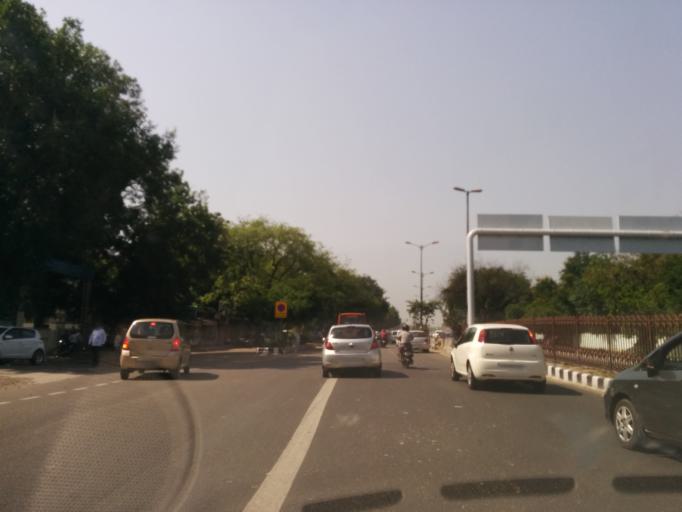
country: IN
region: NCT
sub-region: New Delhi
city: New Delhi
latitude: 28.5638
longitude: 77.2077
